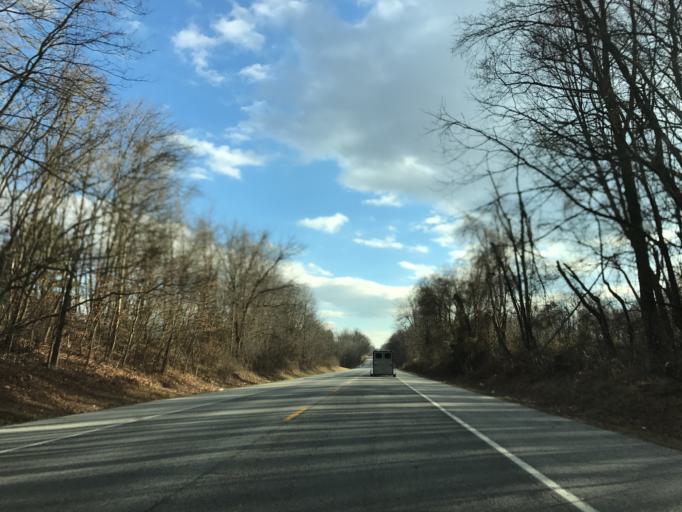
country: US
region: Maryland
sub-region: Cecil County
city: Rising Sun
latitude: 39.6594
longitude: -76.0750
